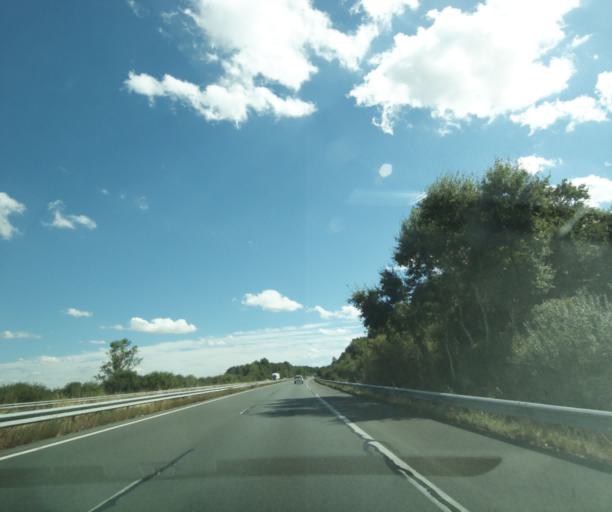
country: FR
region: Aquitaine
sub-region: Departement du Lot-et-Garonne
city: Fourques-sur-Garonne
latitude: 44.4213
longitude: 0.1699
